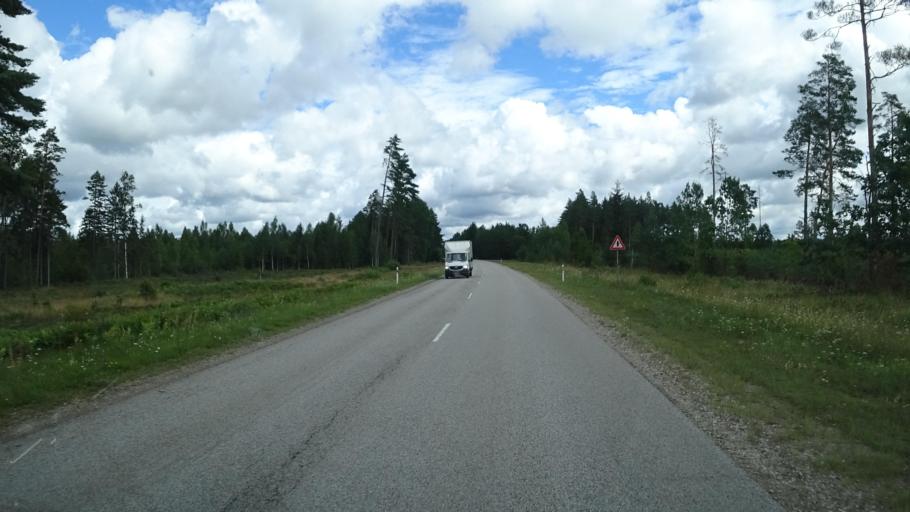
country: LV
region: Pavilostas
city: Pavilosta
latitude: 56.7474
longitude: 21.2484
